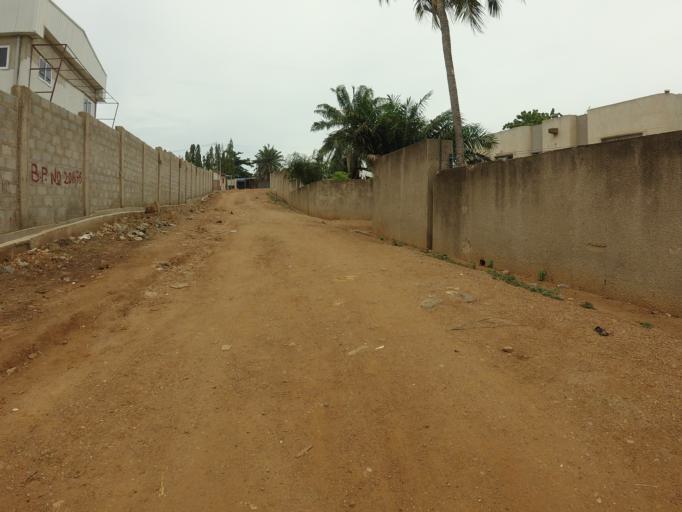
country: GH
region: Greater Accra
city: Dome
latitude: 5.6060
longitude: -0.2247
